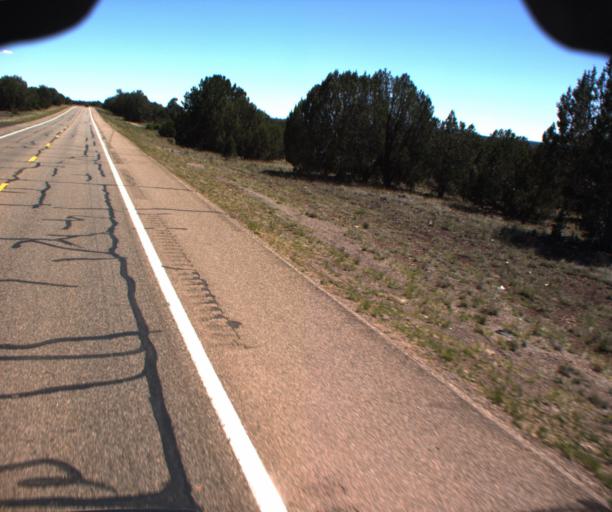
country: US
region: Arizona
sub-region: Yavapai County
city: Paulden
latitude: 35.1143
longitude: -112.4321
